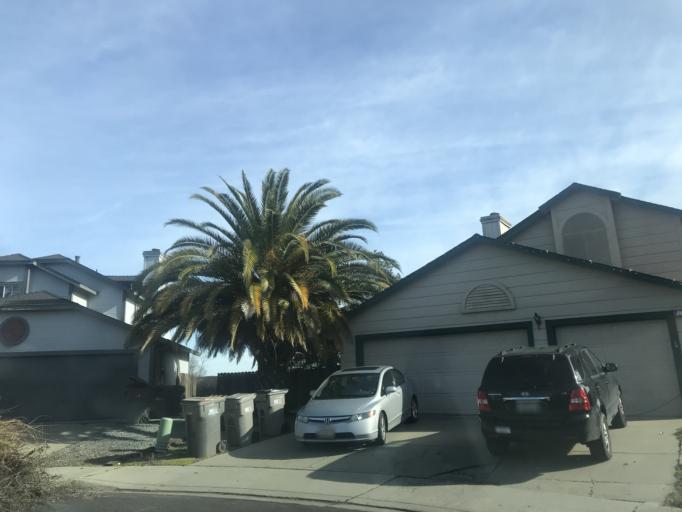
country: US
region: California
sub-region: Yolo County
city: Woodland
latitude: 38.6595
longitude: -121.7533
